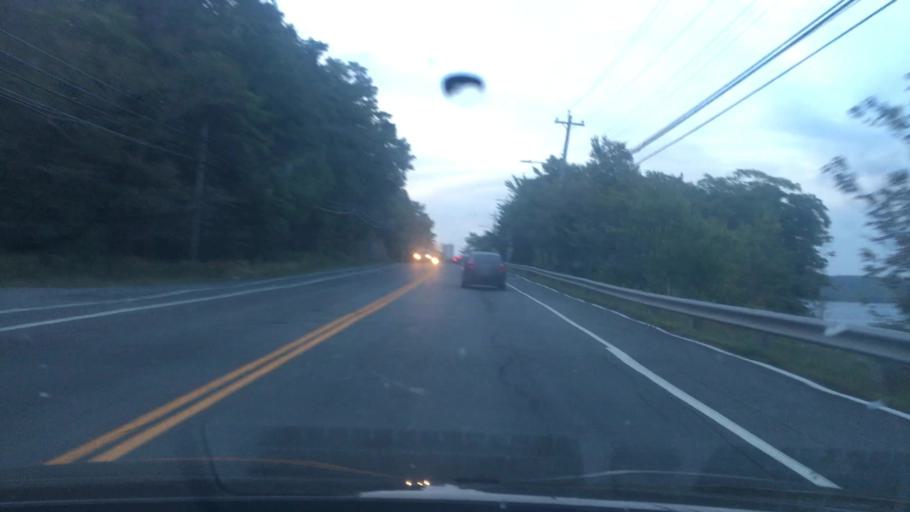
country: CA
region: Nova Scotia
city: Dartmouth
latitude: 44.6895
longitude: -63.6595
